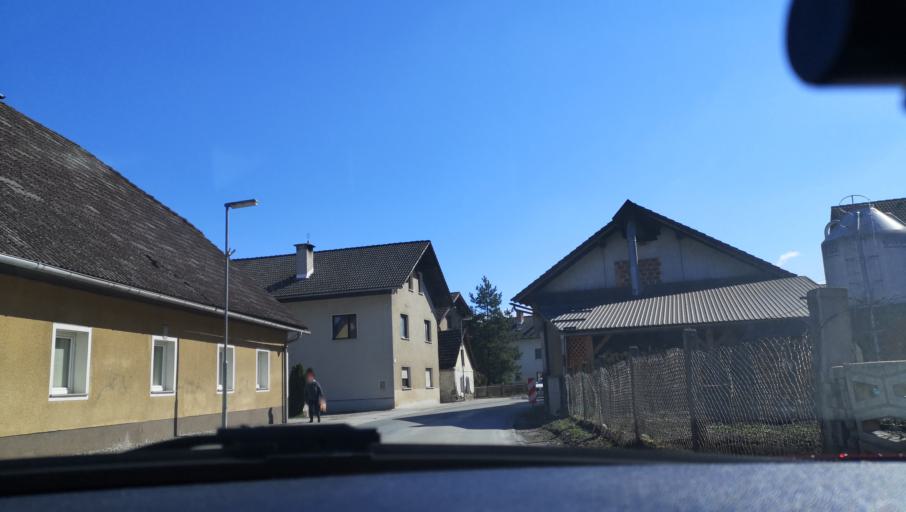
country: SI
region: Ig
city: Ig
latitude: 45.9604
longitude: 14.5245
